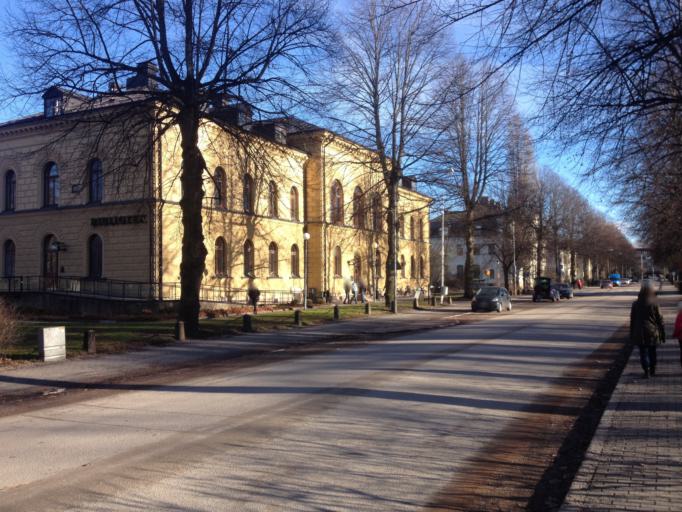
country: SE
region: Vaestra Goetaland
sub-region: Mariestads Kommun
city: Mariestad
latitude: 58.7072
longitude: 13.8245
